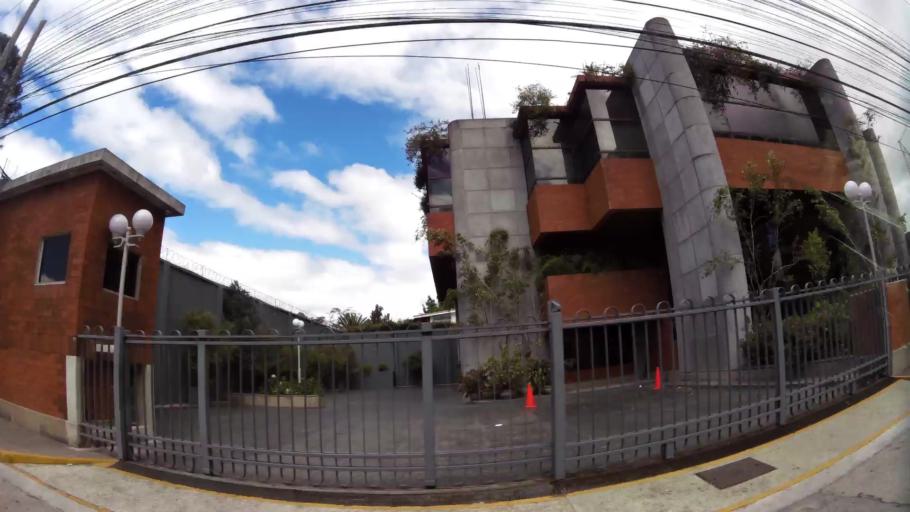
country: GT
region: Guatemala
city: Guatemala City
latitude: 14.6070
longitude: -90.5113
